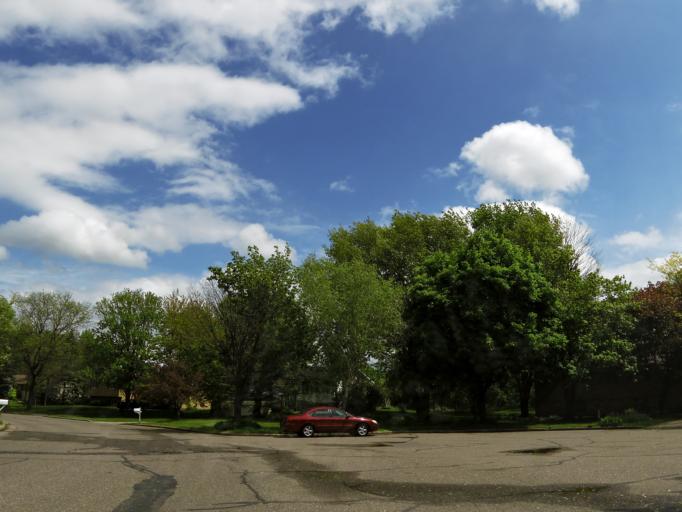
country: US
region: Wisconsin
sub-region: Saint Croix County
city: Hudson
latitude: 44.9819
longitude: -92.7323
